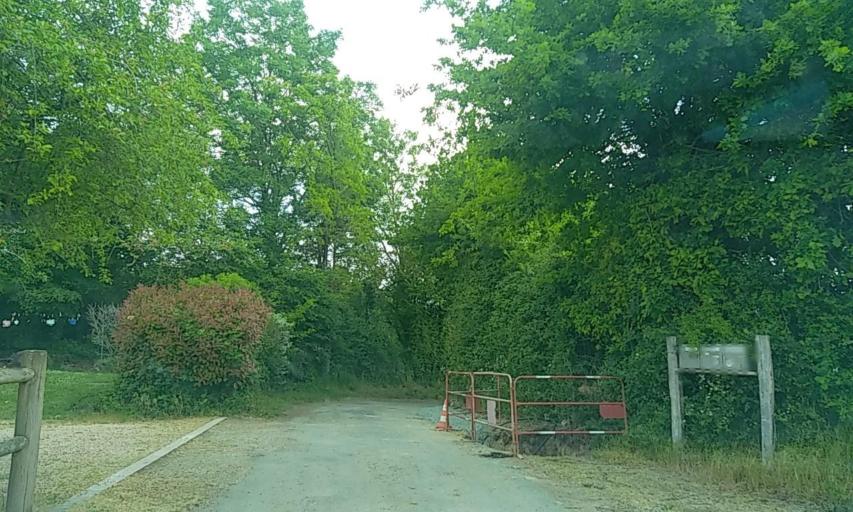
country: FR
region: Poitou-Charentes
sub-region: Departement des Deux-Sevres
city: Boisme
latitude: 46.7589
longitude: -0.4359
